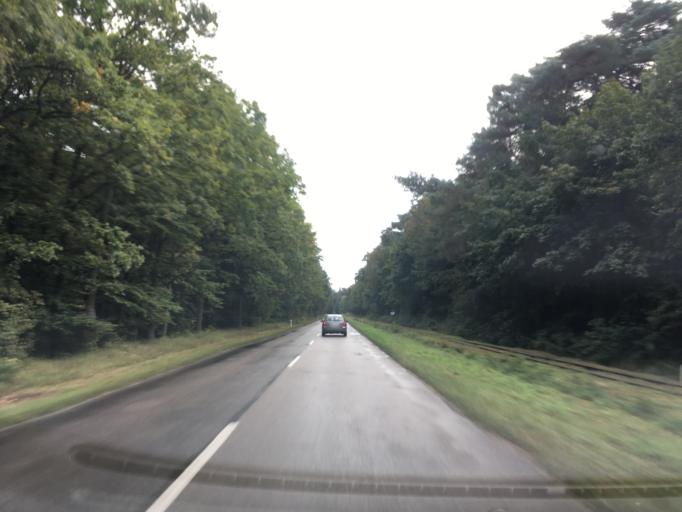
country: PL
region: Pomeranian Voivodeship
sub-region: Powiat nowodworski
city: Stegna
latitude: 54.3326
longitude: 19.0633
